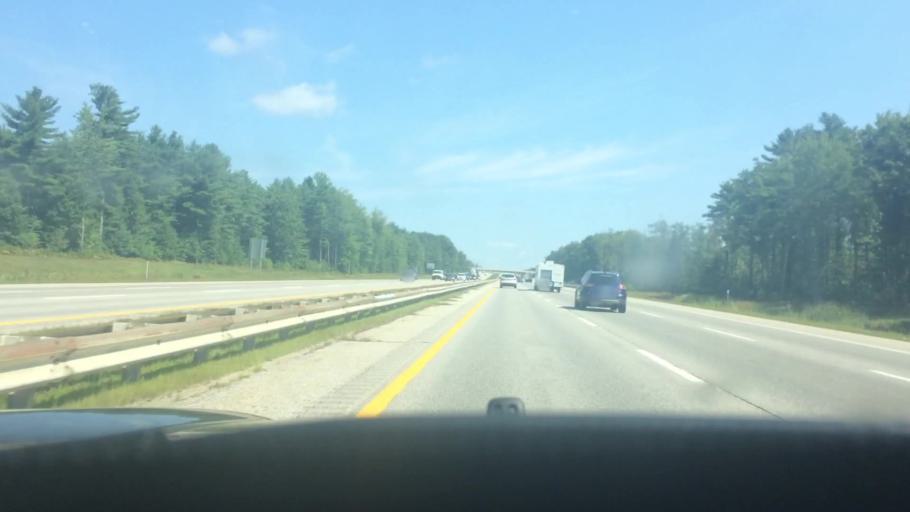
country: US
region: Maine
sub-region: Cumberland County
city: West Scarborough
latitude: 43.5484
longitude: -70.4306
